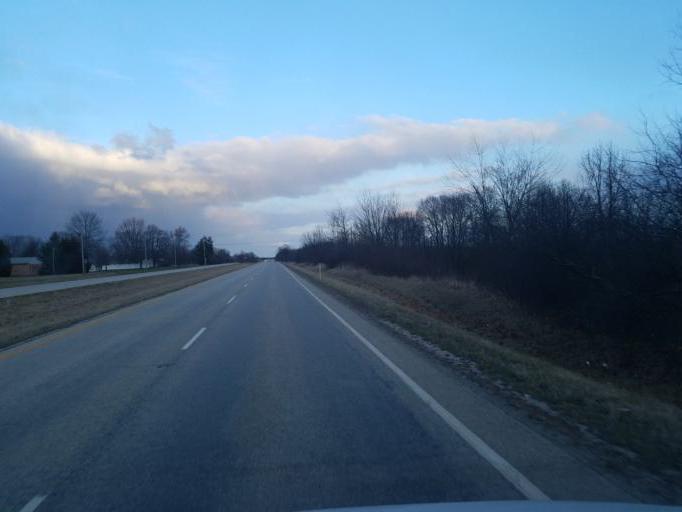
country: US
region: Indiana
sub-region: Henry County
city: Knightstown
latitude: 39.8021
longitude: -85.4833
